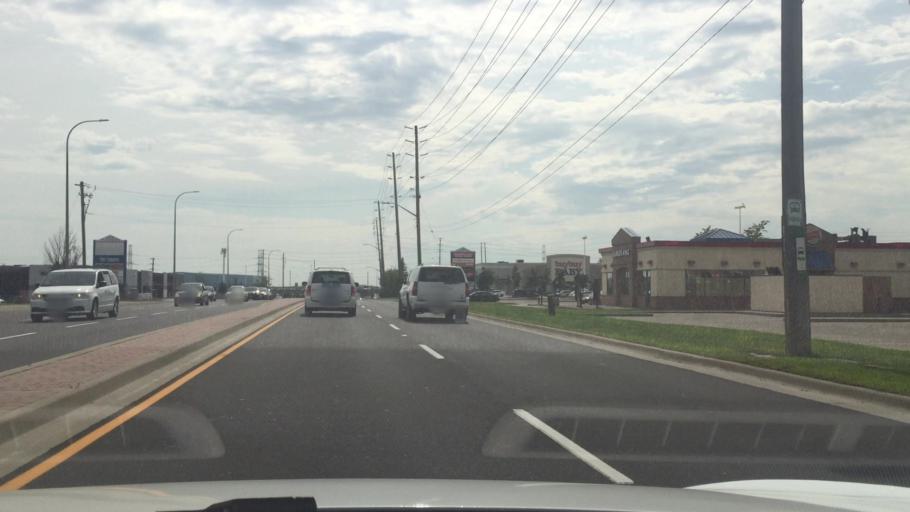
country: CA
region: Ontario
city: Oshawa
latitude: 43.8672
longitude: -78.9002
